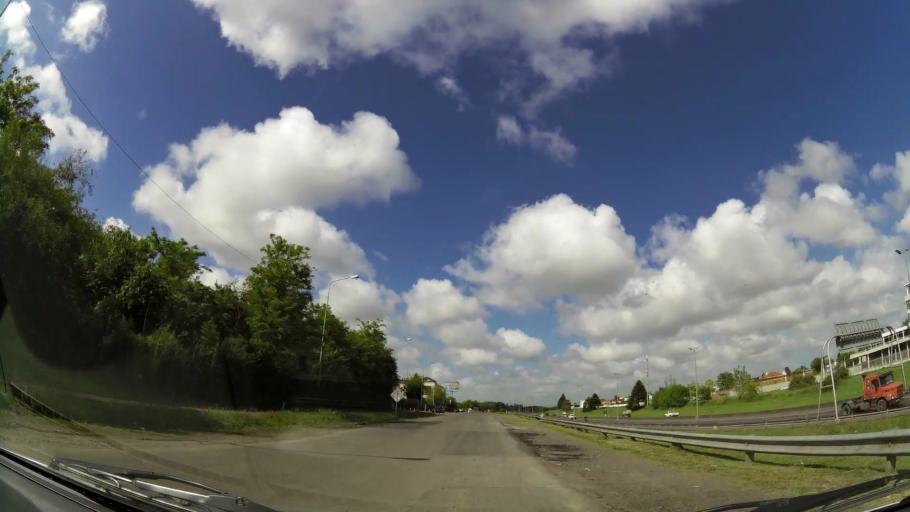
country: AR
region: Buenos Aires
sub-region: Partido de Quilmes
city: Quilmes
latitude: -34.7950
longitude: -58.1593
